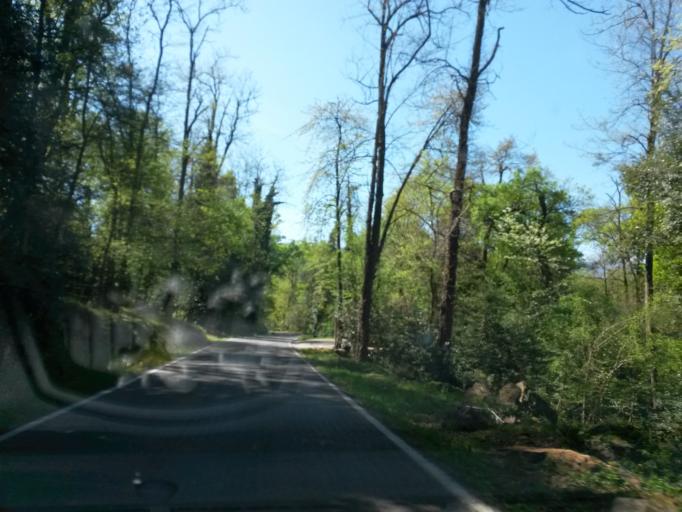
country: ES
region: Catalonia
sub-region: Provincia de Girona
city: Sant Cristofol de les Fonts
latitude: 42.1718
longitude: 2.5035
